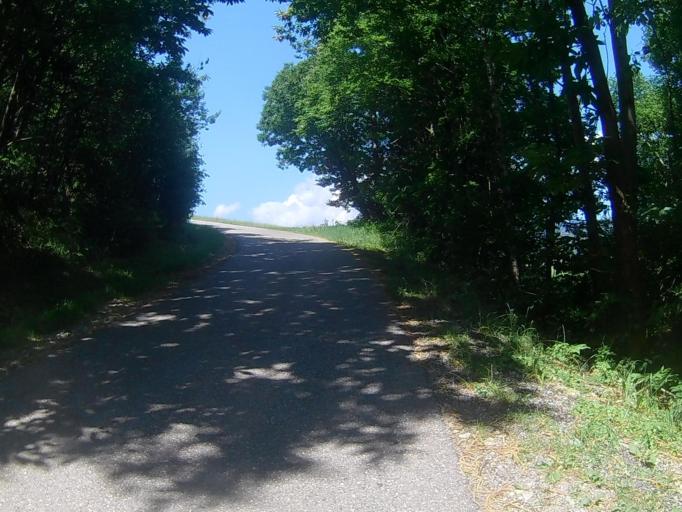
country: SI
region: Race-Fram
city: Fram
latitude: 46.4782
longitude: 15.6037
